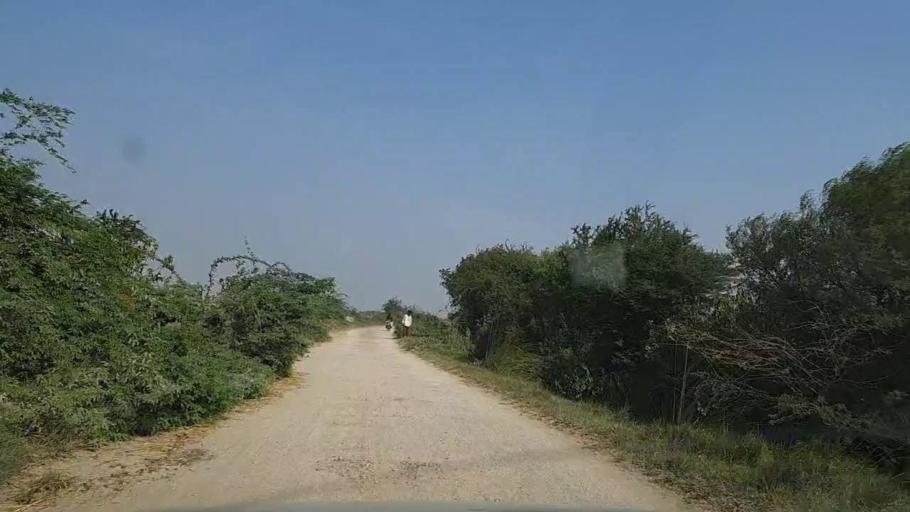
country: PK
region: Sindh
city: Mirpur Sakro
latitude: 24.5598
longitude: 67.6037
